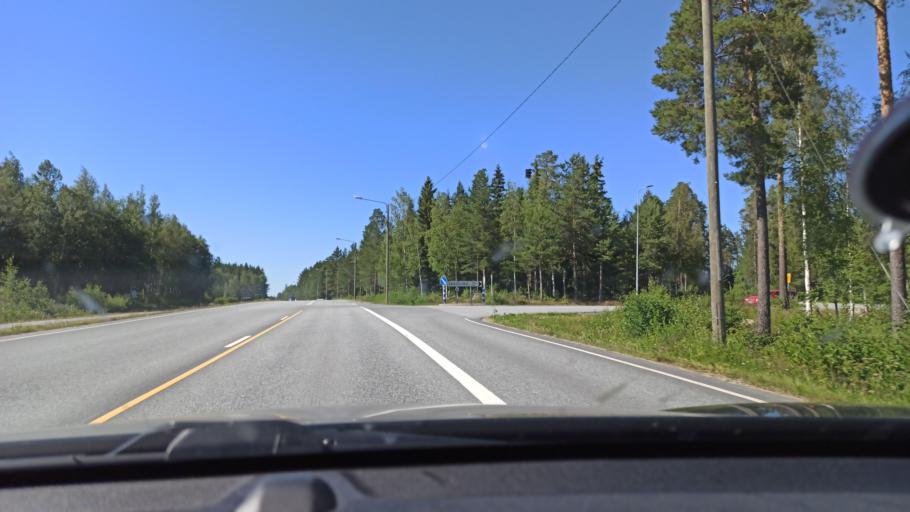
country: FI
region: Ostrobothnia
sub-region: Jakobstadsregionen
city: Jakobstad
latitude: 63.6431
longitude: 22.7361
